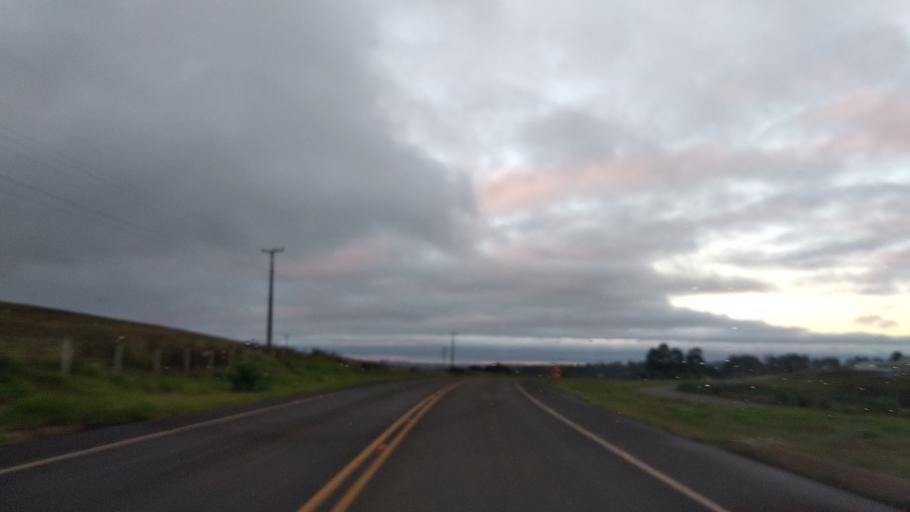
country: BR
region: Santa Catarina
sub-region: Campos Novos
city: Campos Novos
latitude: -27.3709
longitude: -51.2033
